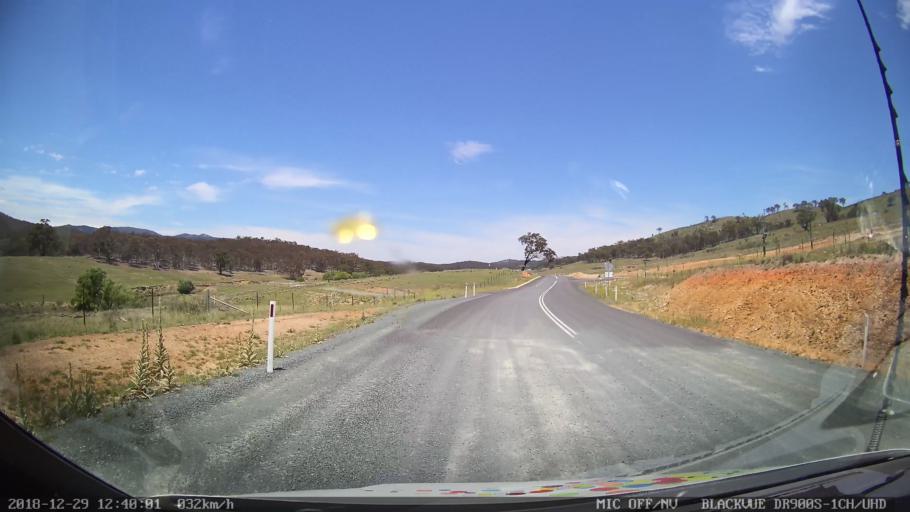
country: AU
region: Australian Capital Territory
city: Macarthur
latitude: -35.5986
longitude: 149.2263
